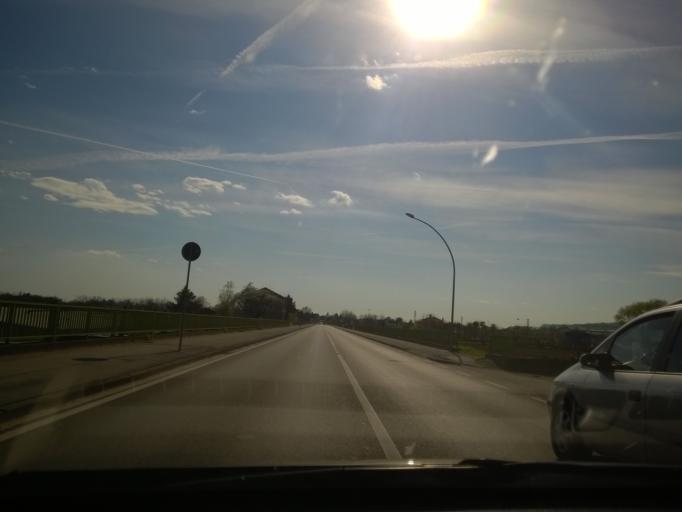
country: IT
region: Veneto
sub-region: Provincia di Treviso
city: Giavera del Montello
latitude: 45.8009
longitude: 12.1825
